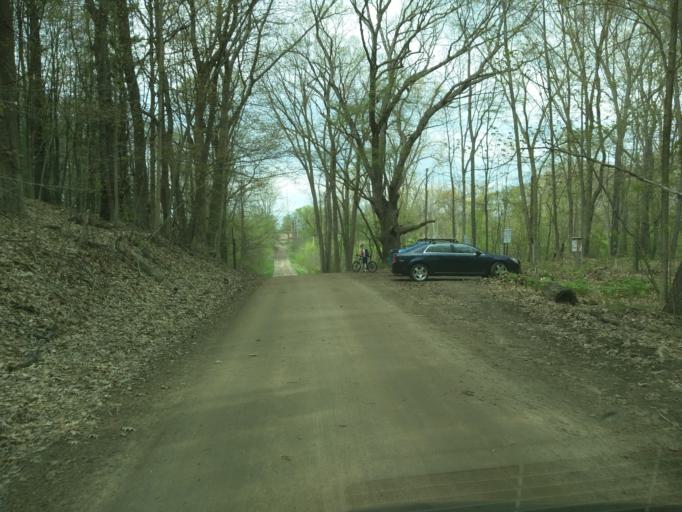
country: US
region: Michigan
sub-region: Eaton County
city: Waverly
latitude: 42.6955
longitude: -84.6227
